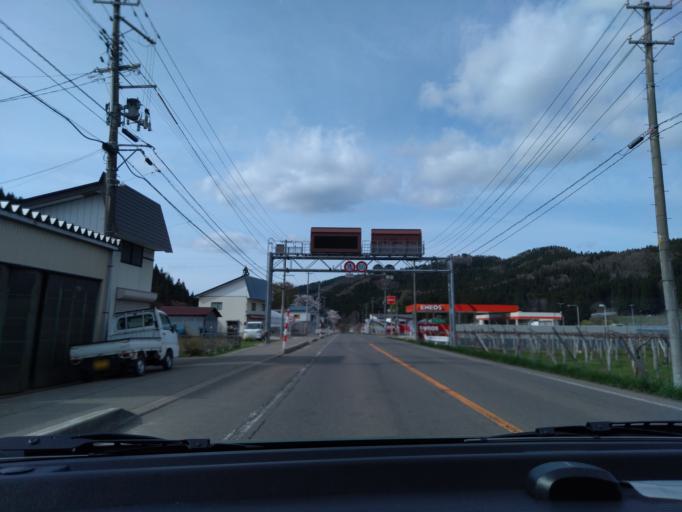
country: JP
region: Akita
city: Yokotemachi
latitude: 39.2940
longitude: 140.5895
